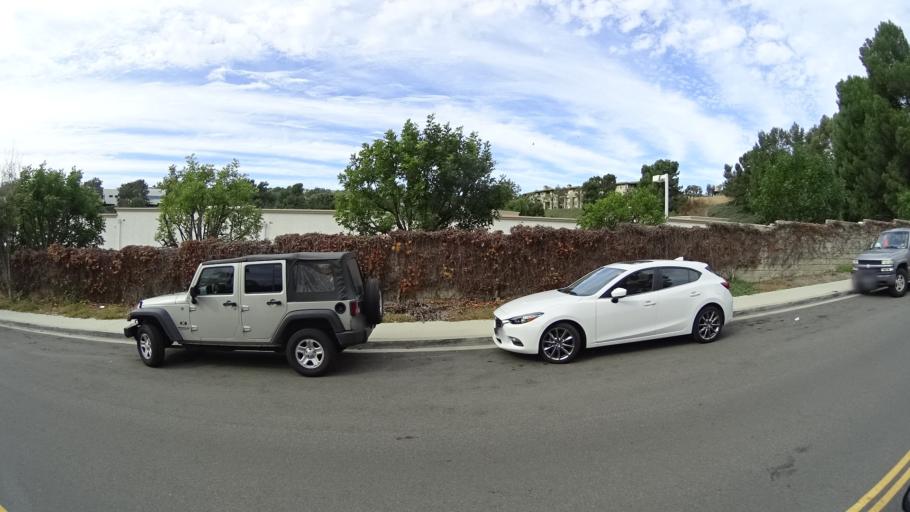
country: US
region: California
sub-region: Orange County
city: Aliso Viejo
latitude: 33.5595
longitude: -117.7232
